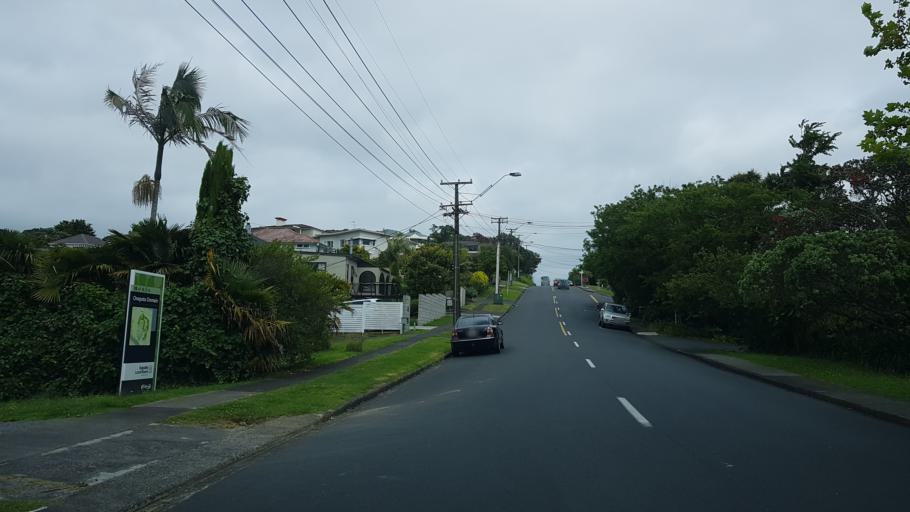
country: NZ
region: Auckland
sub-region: Auckland
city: North Shore
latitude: -36.8049
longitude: 174.7510
